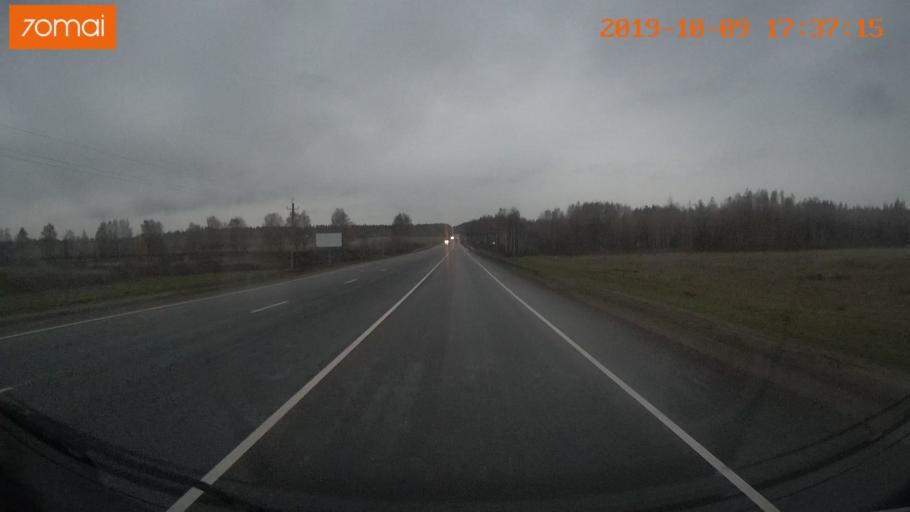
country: RU
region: Ivanovo
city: Bogorodskoye
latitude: 57.0707
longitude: 40.9838
